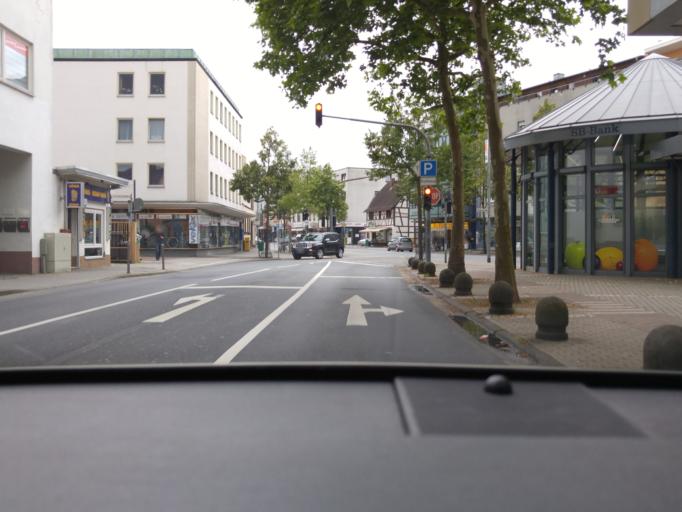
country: DE
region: Hesse
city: Dreieich
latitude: 50.0193
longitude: 8.6961
